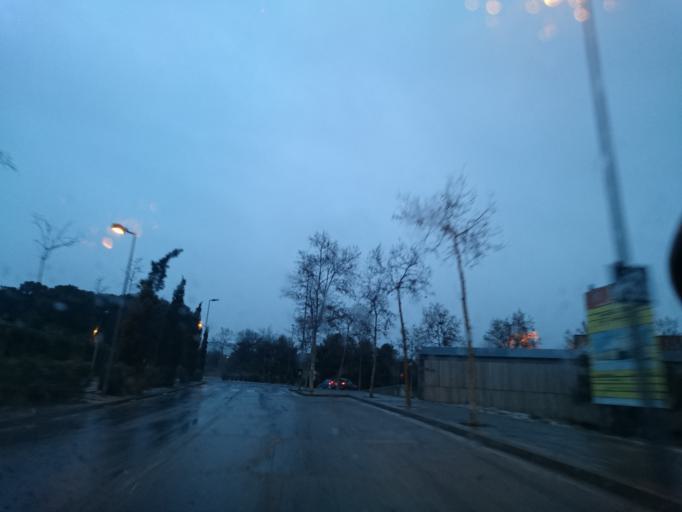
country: ES
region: Catalonia
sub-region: Provincia de Barcelona
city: Vilanova i la Geltru
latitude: 41.2413
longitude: 1.7253
